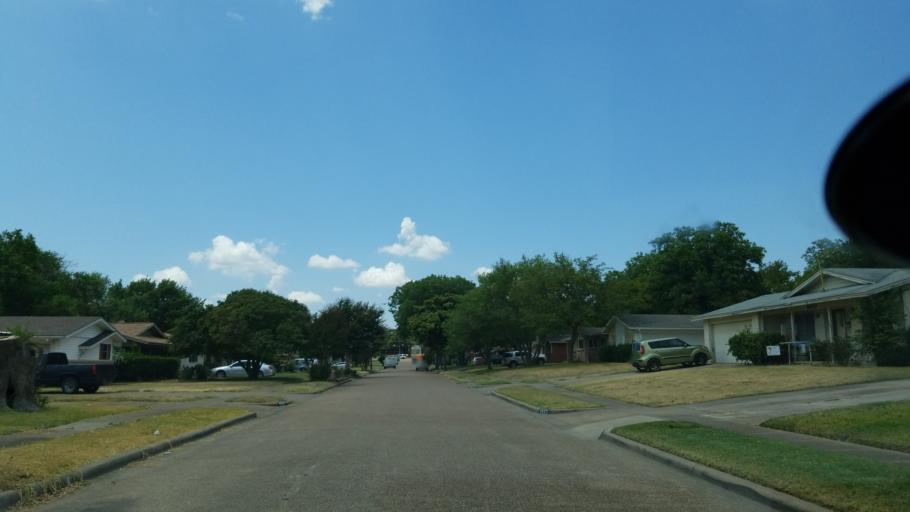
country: US
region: Texas
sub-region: Dallas County
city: Cockrell Hill
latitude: 32.7156
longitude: -96.8972
